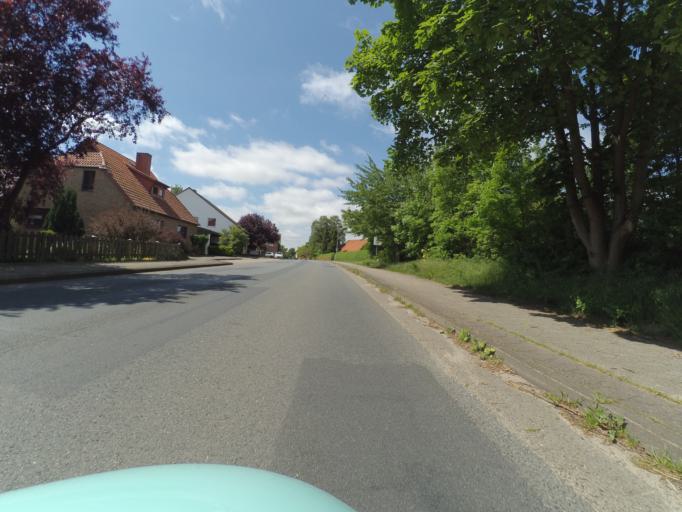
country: DE
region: Lower Saxony
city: Leiferde
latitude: 52.4386
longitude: 10.4434
